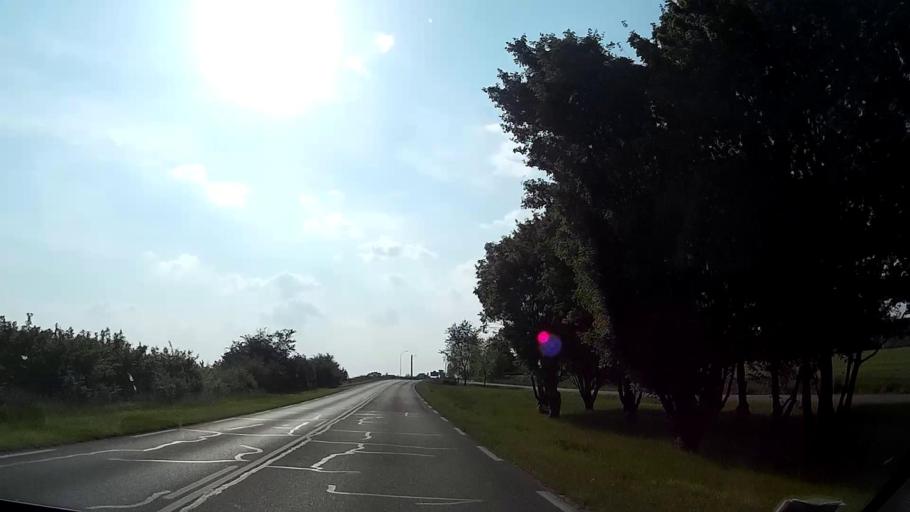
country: FR
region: Centre
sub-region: Departement du Loir-et-Cher
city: Saint-Sulpice-de-Pommeray
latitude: 47.6061
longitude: 1.2794
